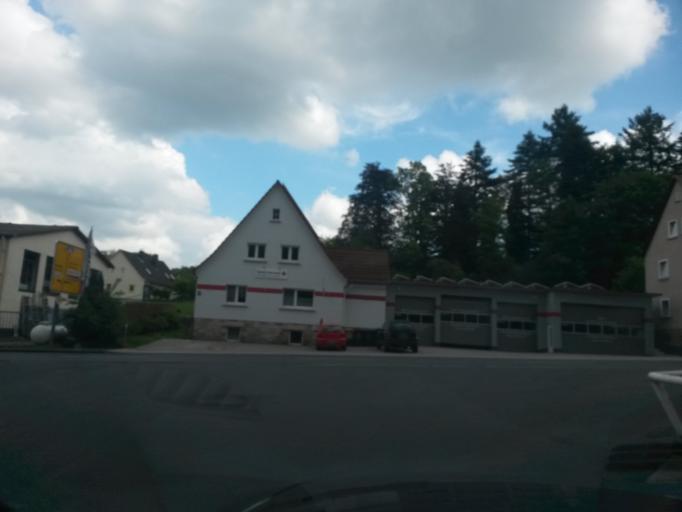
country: DE
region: Hesse
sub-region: Regierungsbezirk Kassel
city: Gersfeld
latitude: 50.4480
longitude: 9.9197
